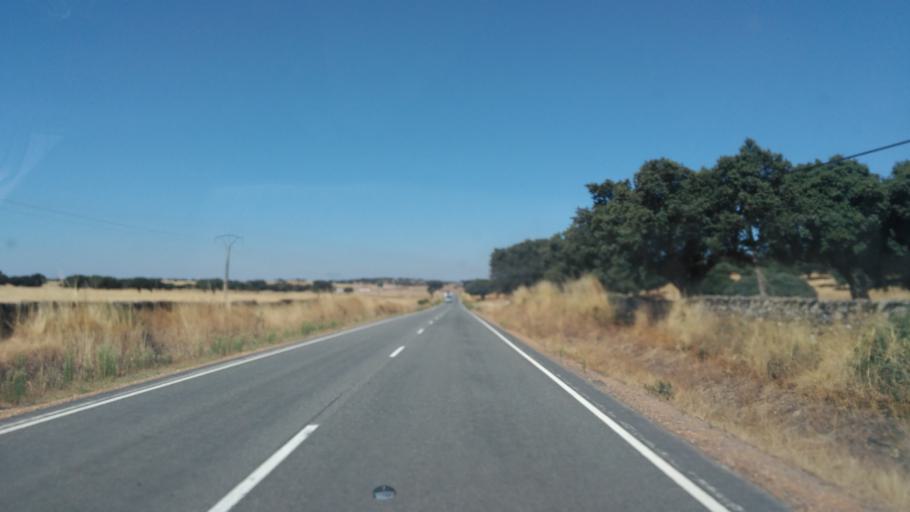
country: ES
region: Castille and Leon
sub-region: Provincia de Salamanca
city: Vecinos
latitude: 40.7900
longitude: -5.9068
